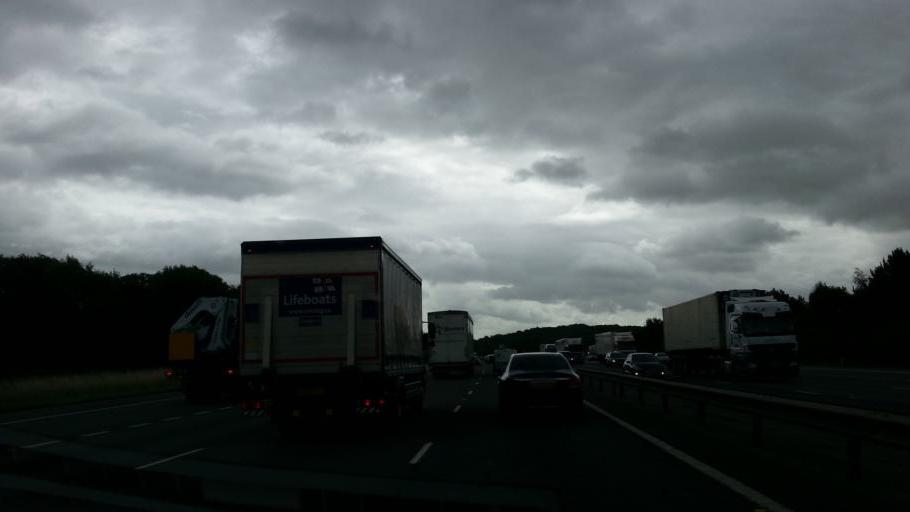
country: GB
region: England
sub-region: Warwickshire
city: Harbury
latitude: 52.2205
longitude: -1.5092
